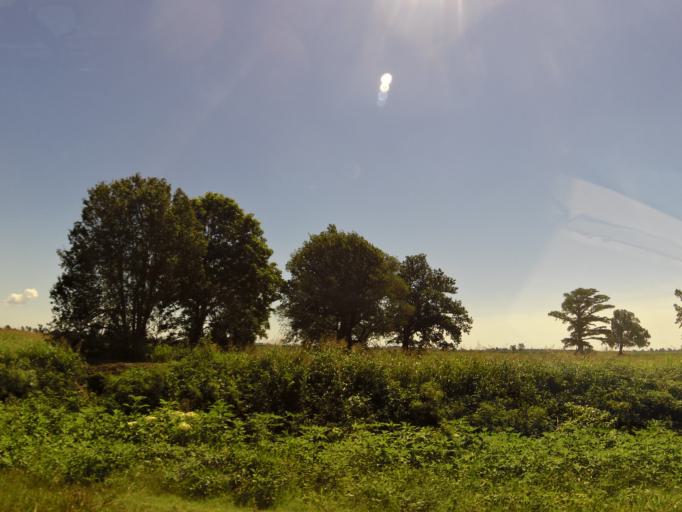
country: US
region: Missouri
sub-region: New Madrid County
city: Lilbourn
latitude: 36.5692
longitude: -89.7027
